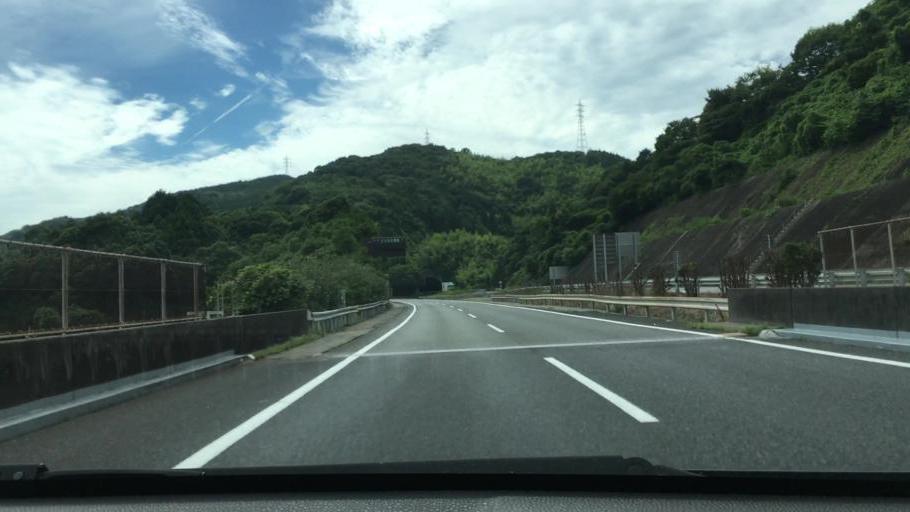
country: JP
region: Yamaguchi
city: Hofu
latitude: 34.0726
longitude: 131.6762
